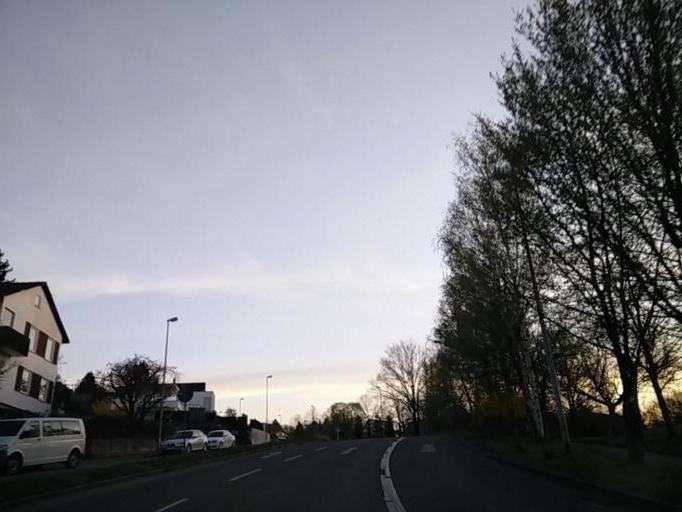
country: DE
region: Baden-Wuerttemberg
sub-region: Tuebingen Region
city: Tuebingen
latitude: 48.5308
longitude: 9.0528
